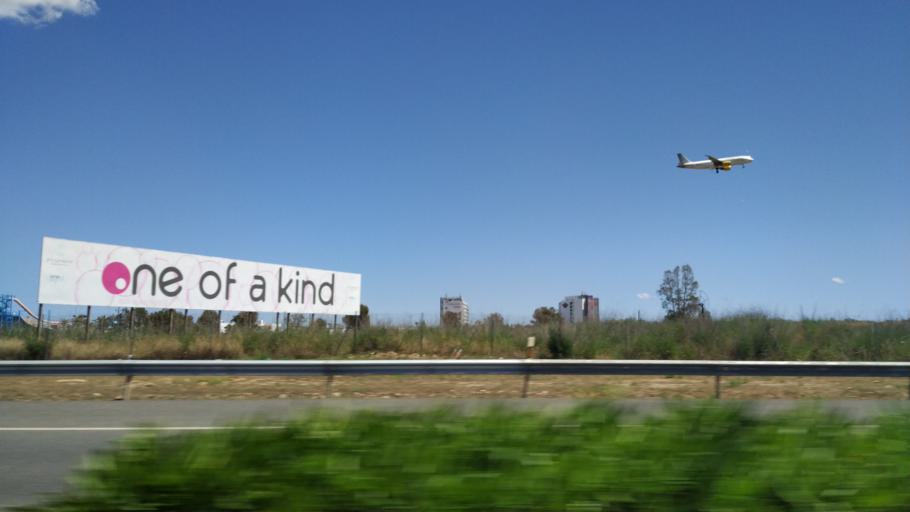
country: ES
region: Balearic Islands
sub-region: Illes Balears
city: Ibiza
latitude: 38.8880
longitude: 1.3997
